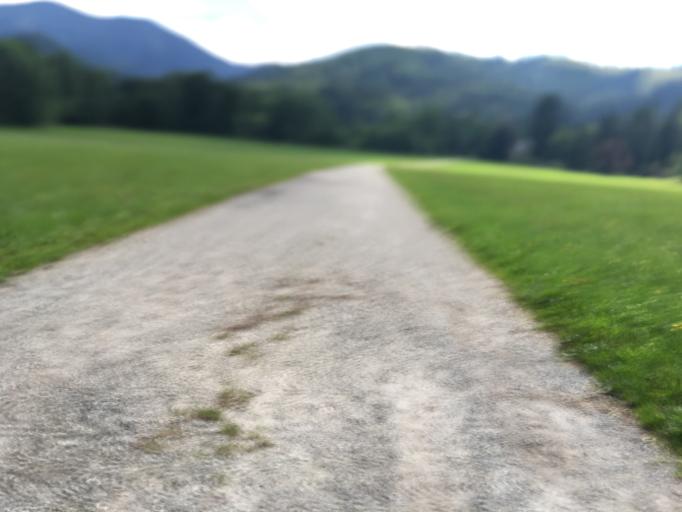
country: AT
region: Lower Austria
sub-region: Politischer Bezirk Lilienfeld
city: Mitterbach am Erlaufsee
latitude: 47.7947
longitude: 15.2585
